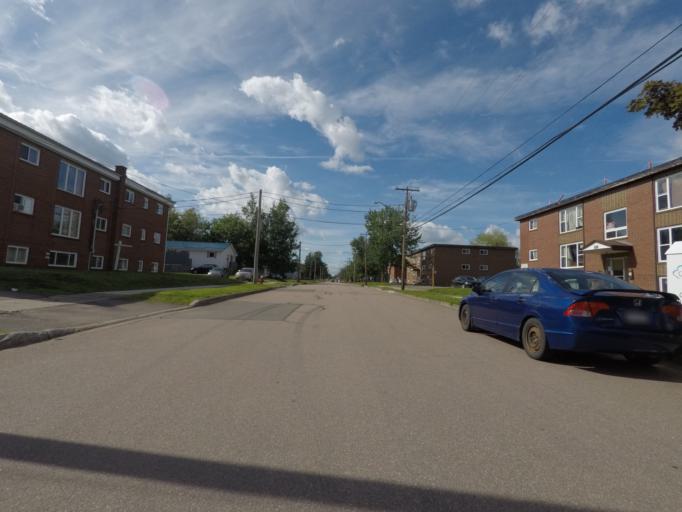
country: CA
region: New Brunswick
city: Moncton
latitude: 46.0968
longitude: -64.8217
